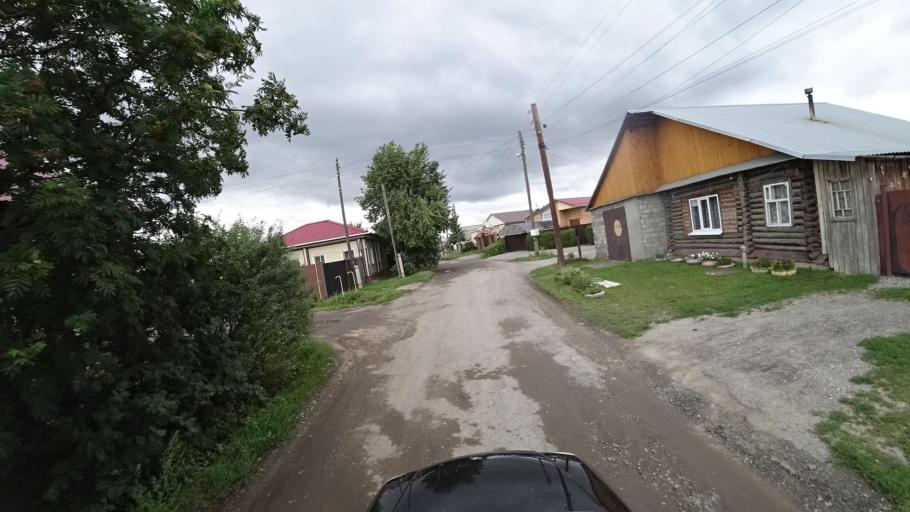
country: RU
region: Sverdlovsk
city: Kamyshlov
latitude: 56.8485
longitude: 62.6816
